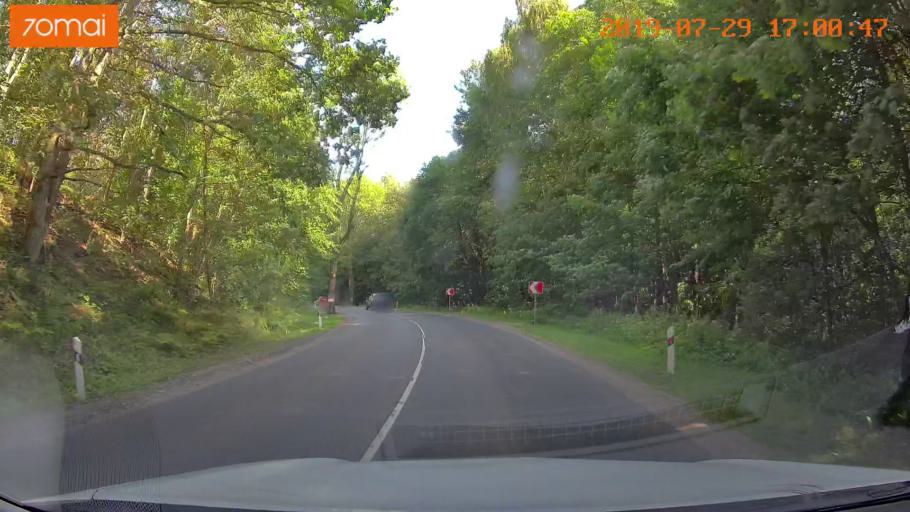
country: RU
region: Kaliningrad
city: Volochayevskoye
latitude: 54.8181
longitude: 20.2307
